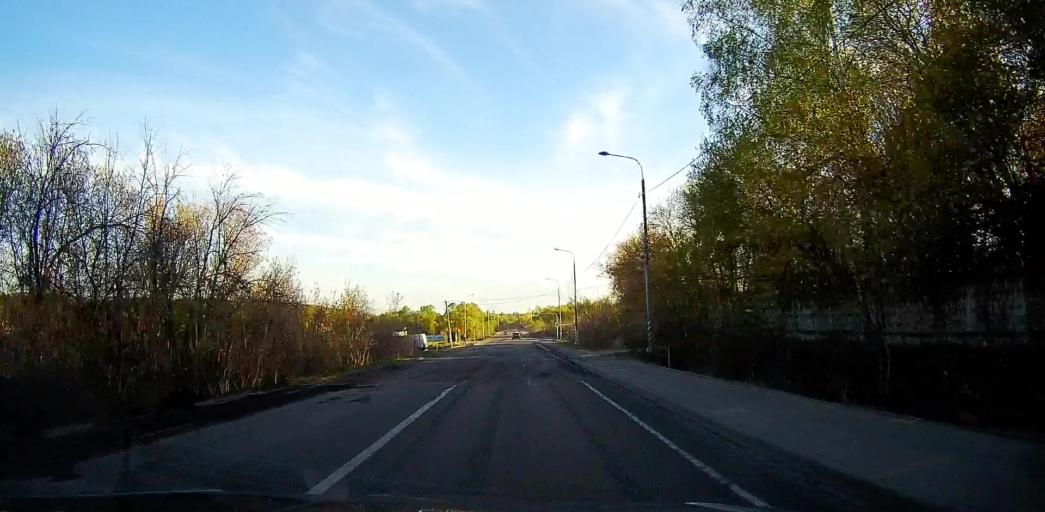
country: RU
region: Moskovskaya
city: Bronnitsy
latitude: 55.3093
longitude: 38.2137
